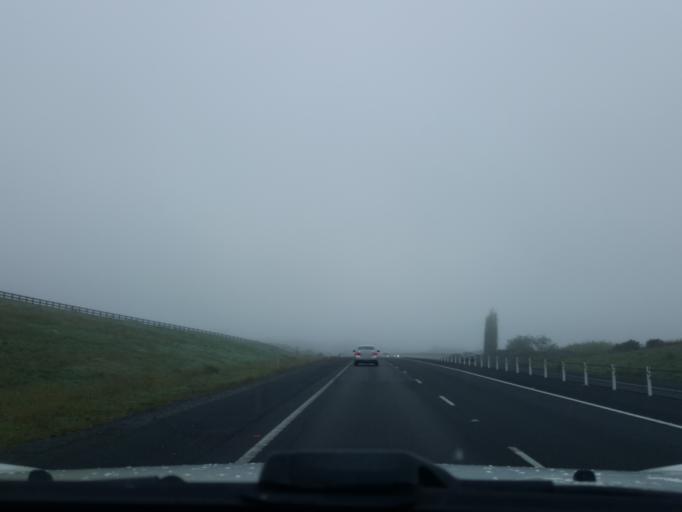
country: NZ
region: Waikato
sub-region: Waikato District
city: Ngaruawahia
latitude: -37.6956
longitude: 175.2123
